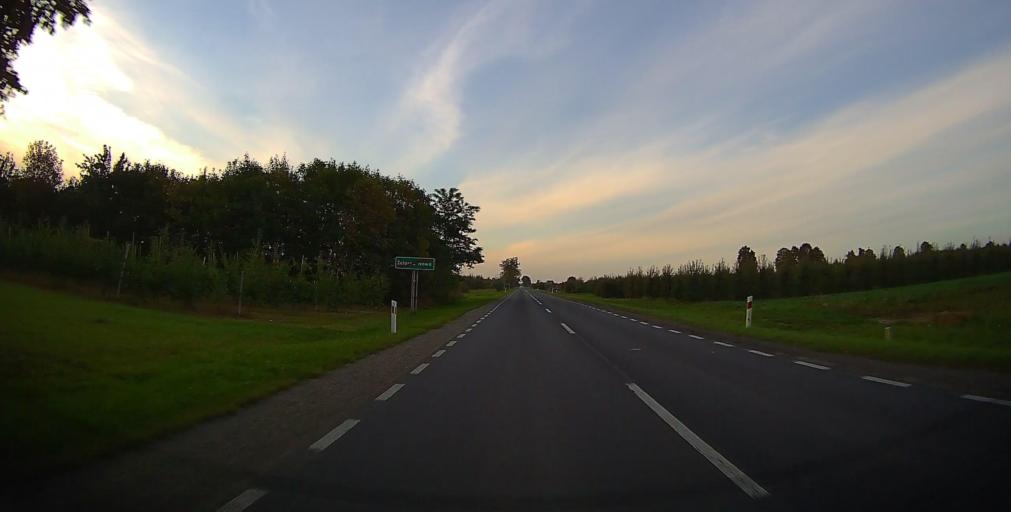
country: PL
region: Masovian Voivodeship
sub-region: Powiat garwolinski
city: Wilga
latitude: 51.8058
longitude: 21.3339
